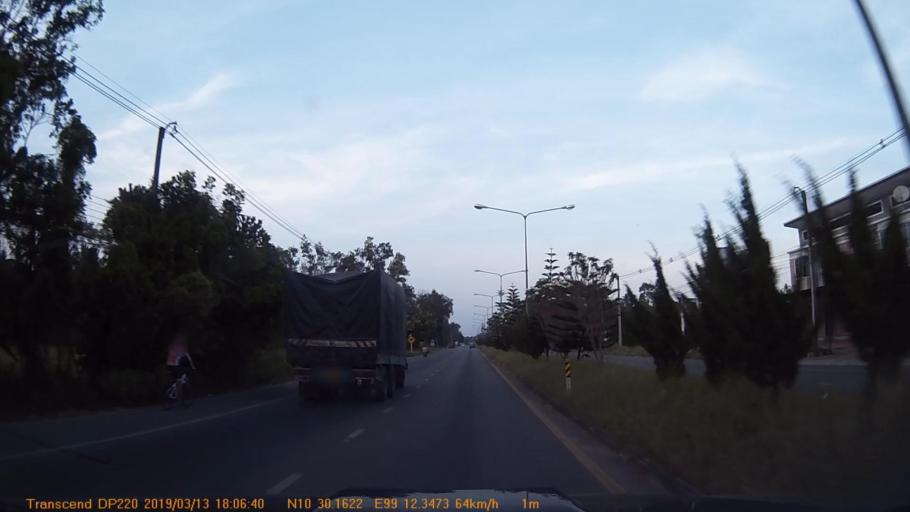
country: TH
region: Chumphon
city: Chumphon
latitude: 10.5029
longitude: 99.2058
